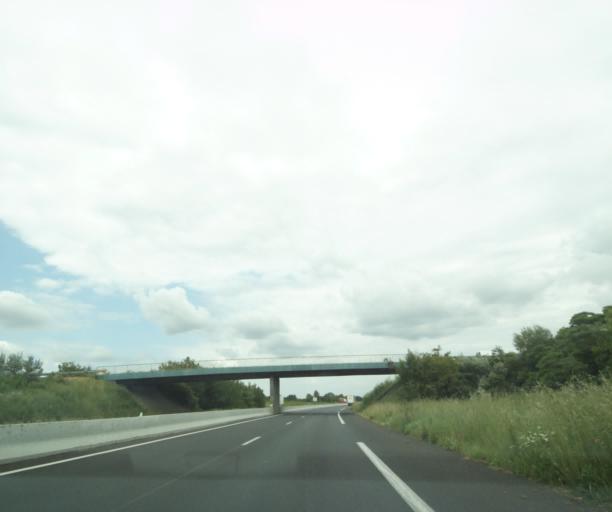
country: FR
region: Pays de la Loire
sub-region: Departement de Maine-et-Loire
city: Saumur
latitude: 47.2803
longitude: -0.0692
